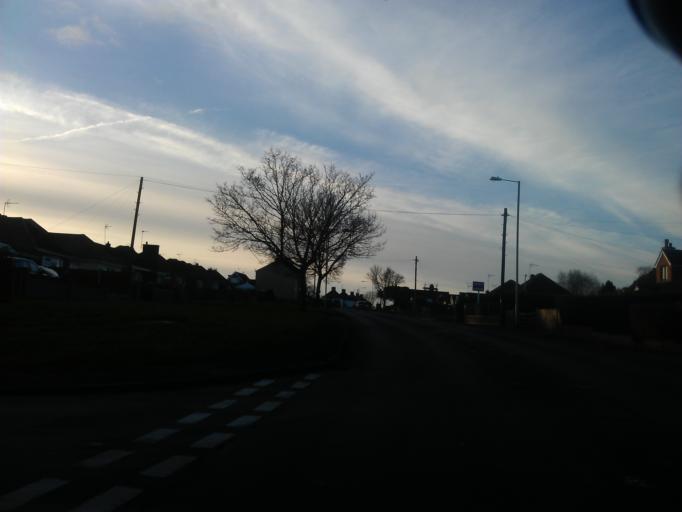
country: GB
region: England
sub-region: Essex
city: Little Clacton
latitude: 51.8097
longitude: 1.1504
